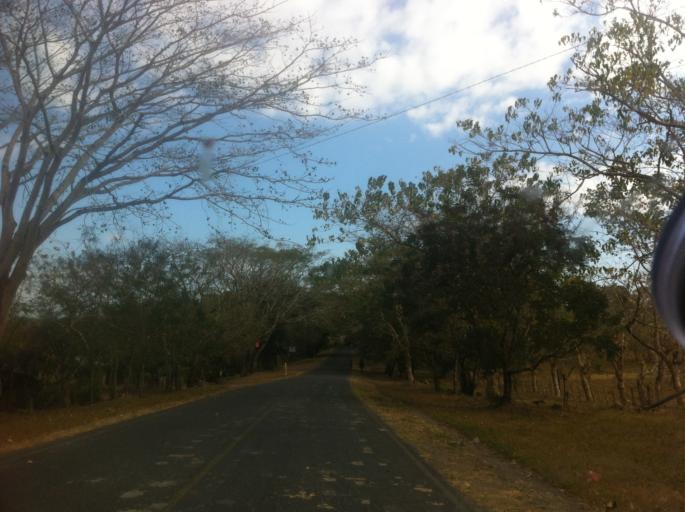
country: NI
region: Rio San Juan
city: San Miguelito
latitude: 11.4088
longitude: -84.9001
